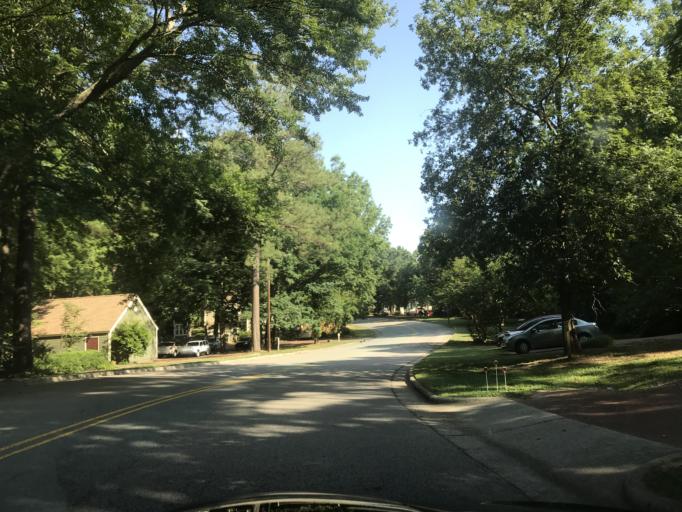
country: US
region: North Carolina
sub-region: Wake County
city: West Raleigh
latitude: 35.8632
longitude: -78.6112
